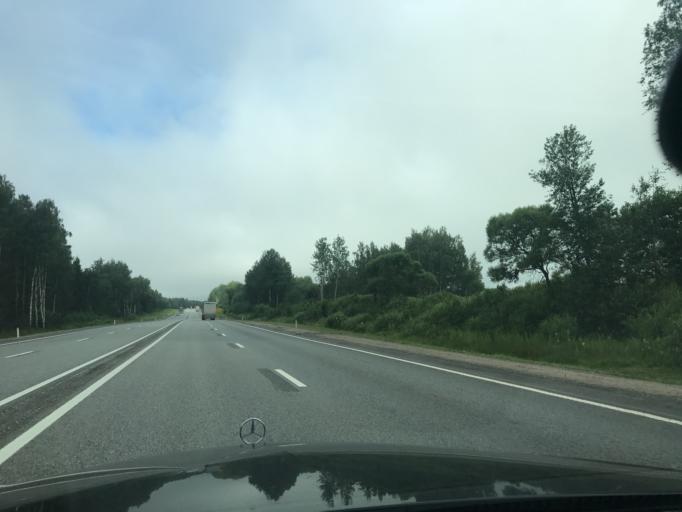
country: RU
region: Smolensk
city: Vyaz'ma
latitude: 55.3301
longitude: 34.5764
